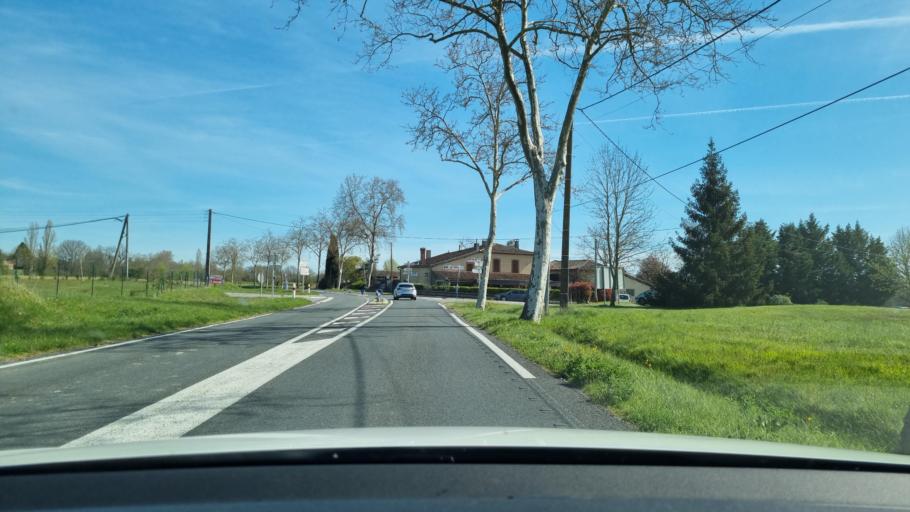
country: FR
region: Midi-Pyrenees
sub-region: Departement du Gers
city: Lombez
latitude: 43.3978
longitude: 0.7936
